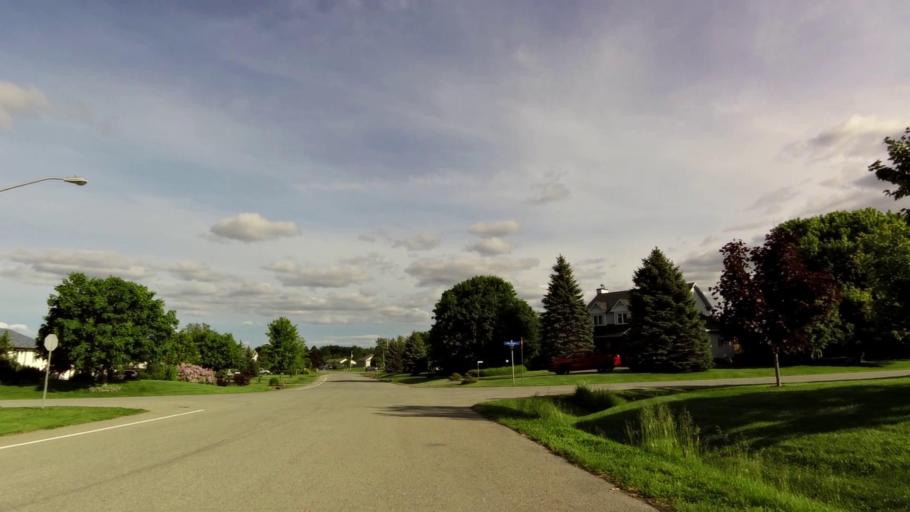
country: CA
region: Ontario
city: Ottawa
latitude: 45.2673
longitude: -75.5682
